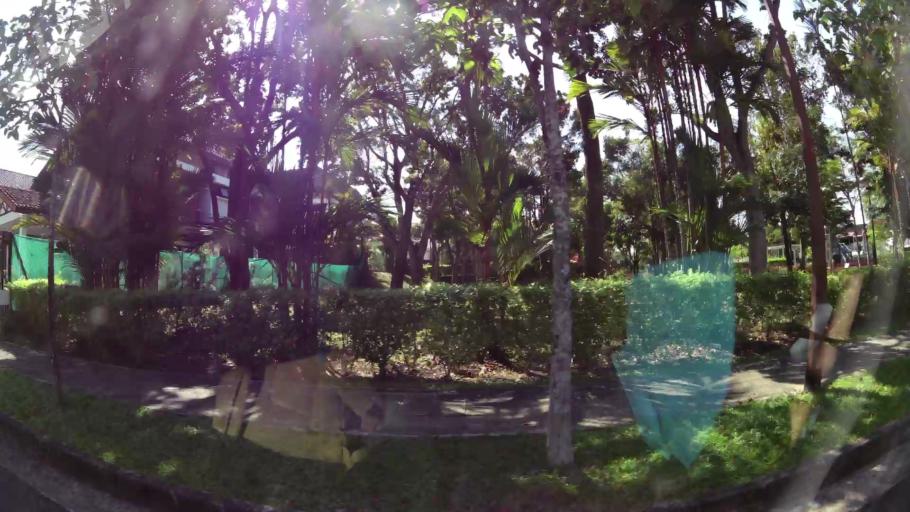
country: SG
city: Singapore
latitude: 1.3792
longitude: 103.8327
